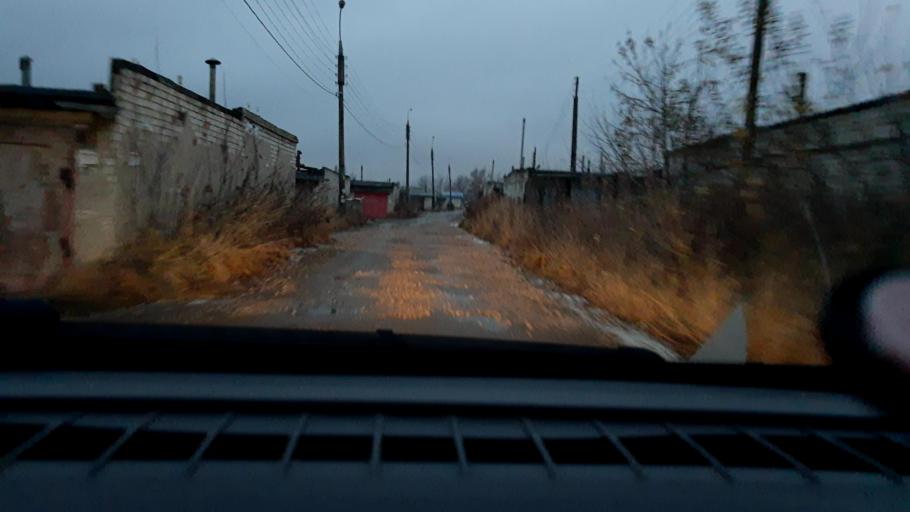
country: RU
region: Nizjnij Novgorod
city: Gorbatovka
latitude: 56.2527
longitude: 43.8375
